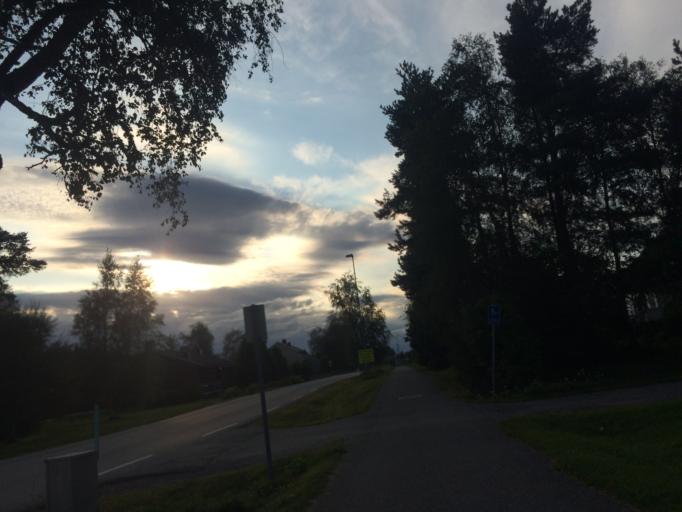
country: NO
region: Akershus
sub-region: Ski
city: Ski
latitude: 59.6821
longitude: 10.8809
